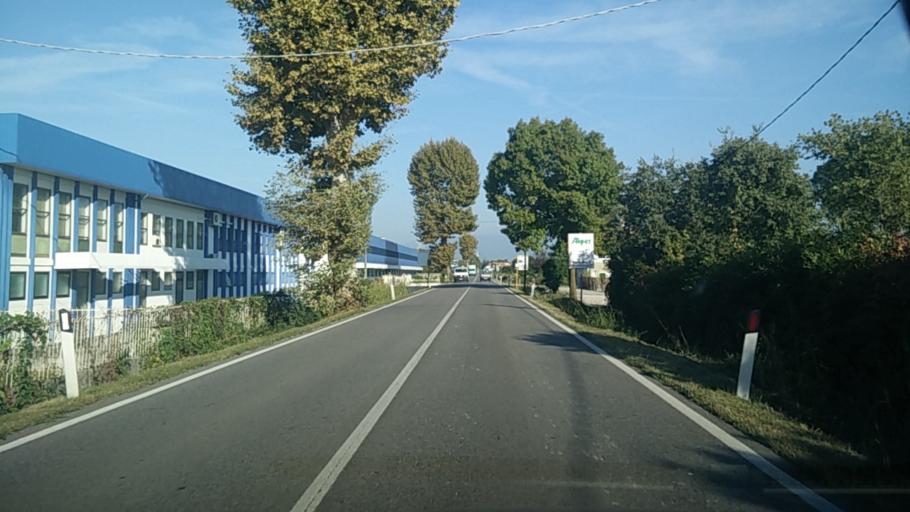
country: IT
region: Veneto
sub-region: Provincia di Treviso
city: Resana
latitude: 45.6489
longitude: 11.9455
